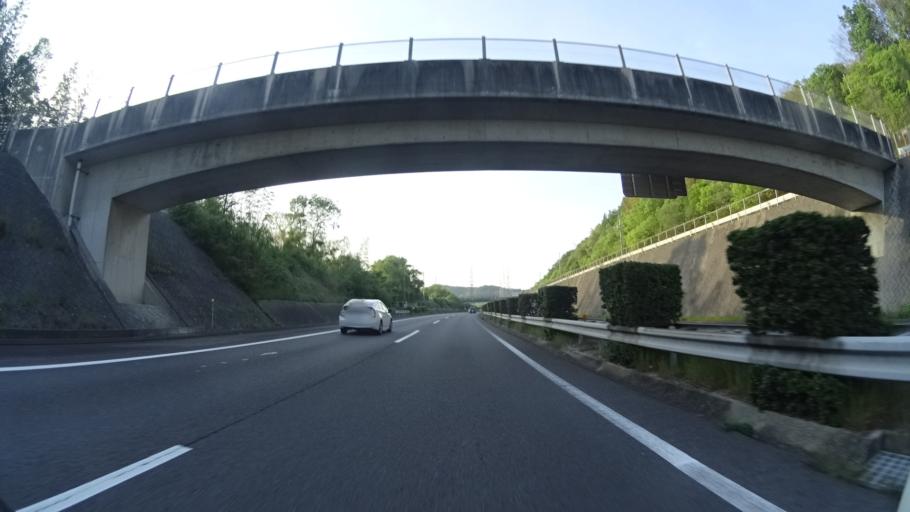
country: JP
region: Kagawa
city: Sakaidecho
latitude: 34.3042
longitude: 133.8405
